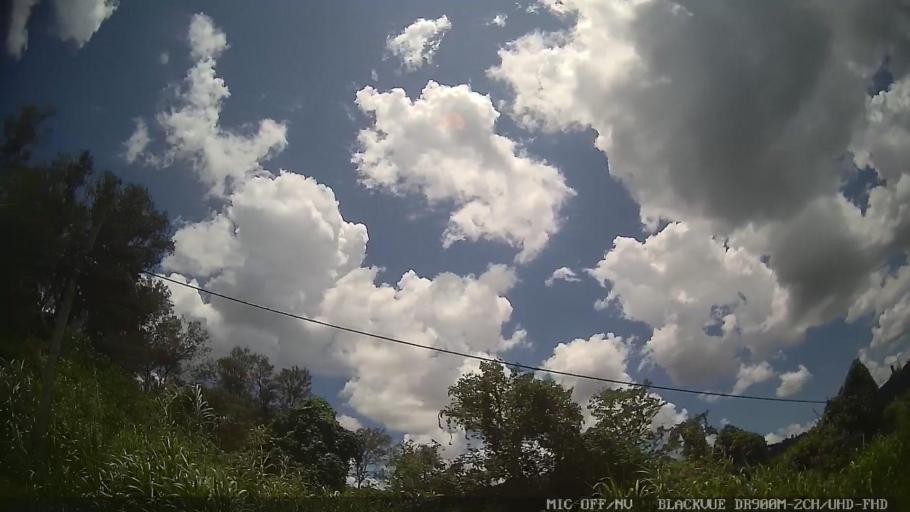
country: BR
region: Sao Paulo
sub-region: Amparo
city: Amparo
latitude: -22.6751
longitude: -46.7398
